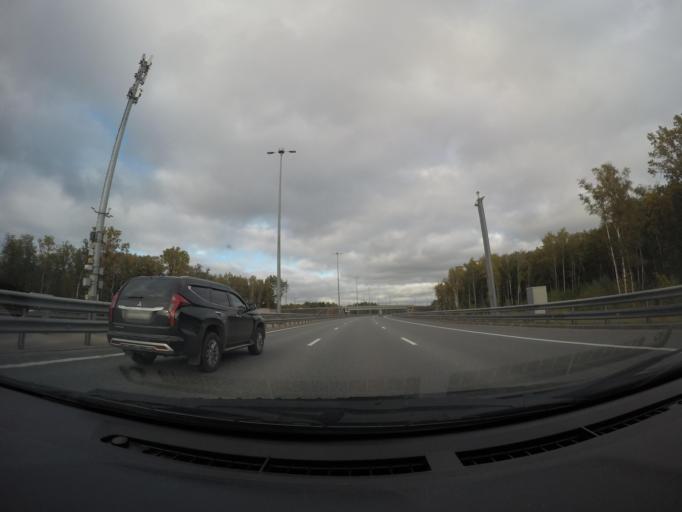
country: RU
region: Moskovskaya
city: Lesnoy Gorodok
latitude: 55.6760
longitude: 37.2273
